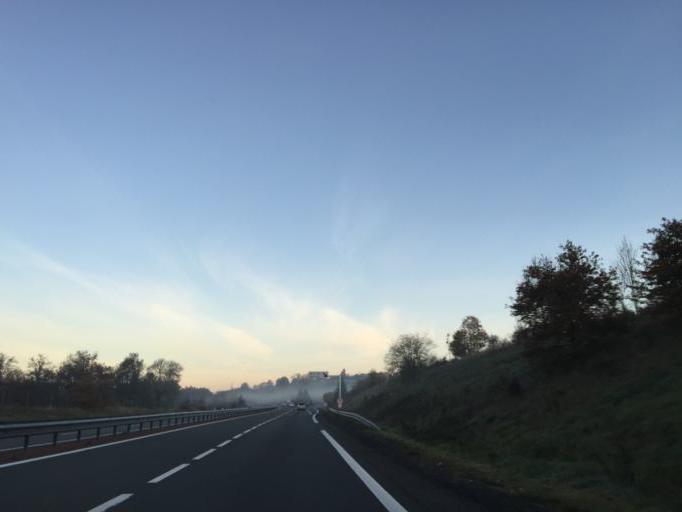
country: FR
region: Rhone-Alpes
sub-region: Departement de la Loire
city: Neulise
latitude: 45.8937
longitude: 4.1734
